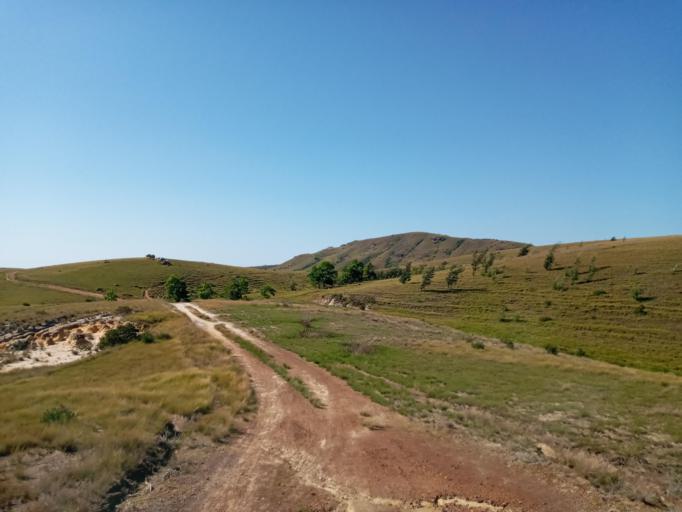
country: MG
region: Anosy
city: Fort Dauphin
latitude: -24.9111
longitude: 47.0717
